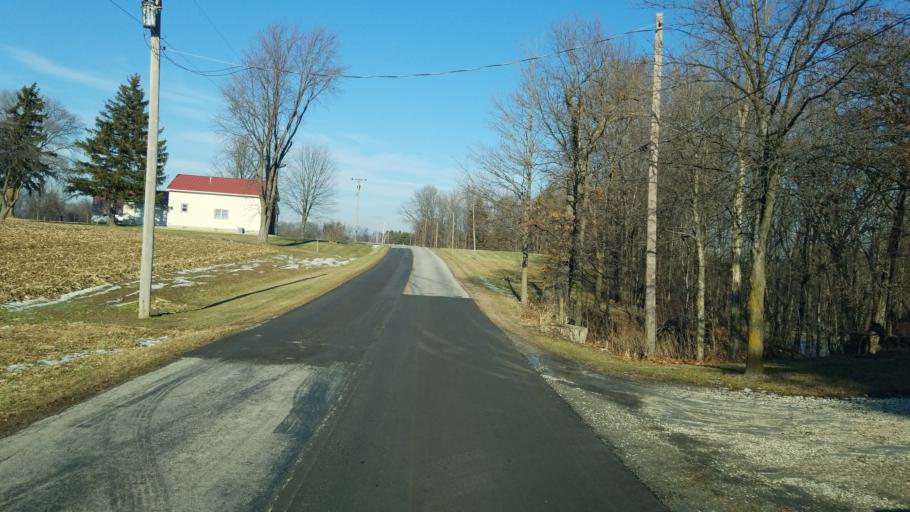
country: US
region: Ohio
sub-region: Huron County
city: Monroeville
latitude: 41.2676
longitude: -82.6861
